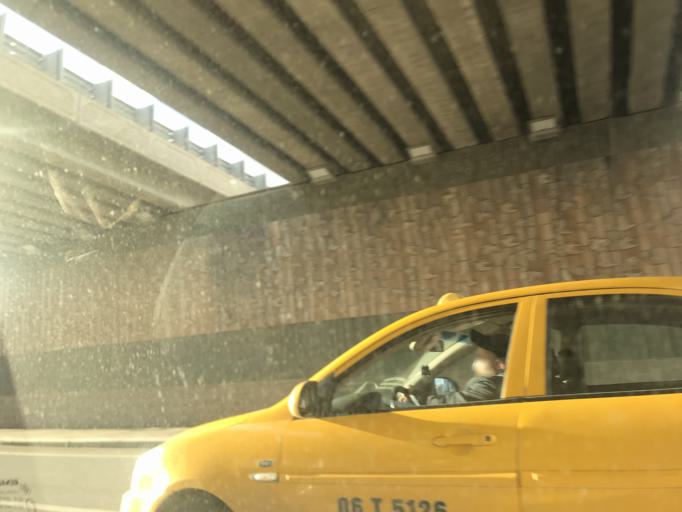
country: TR
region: Ankara
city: Mamak
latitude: 39.9745
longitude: 32.8839
